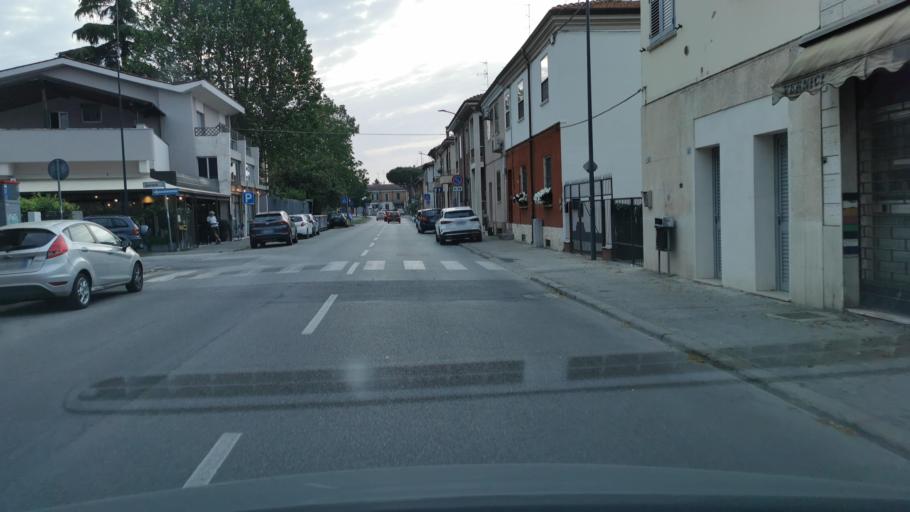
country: IT
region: Emilia-Romagna
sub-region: Provincia di Ravenna
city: Ravenna
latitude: 44.4142
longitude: 12.1909
